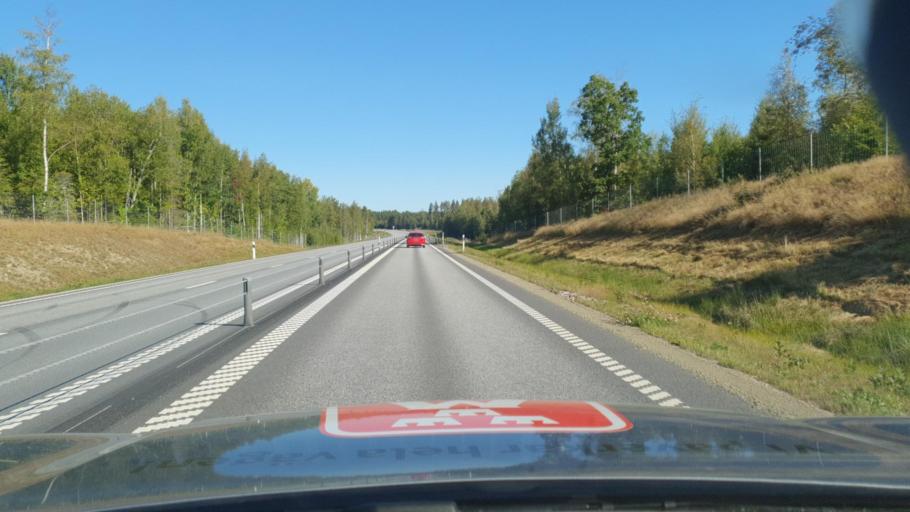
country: SE
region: OErebro
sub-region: Hallsbergs Kommun
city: Palsboda
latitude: 59.0964
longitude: 15.3076
